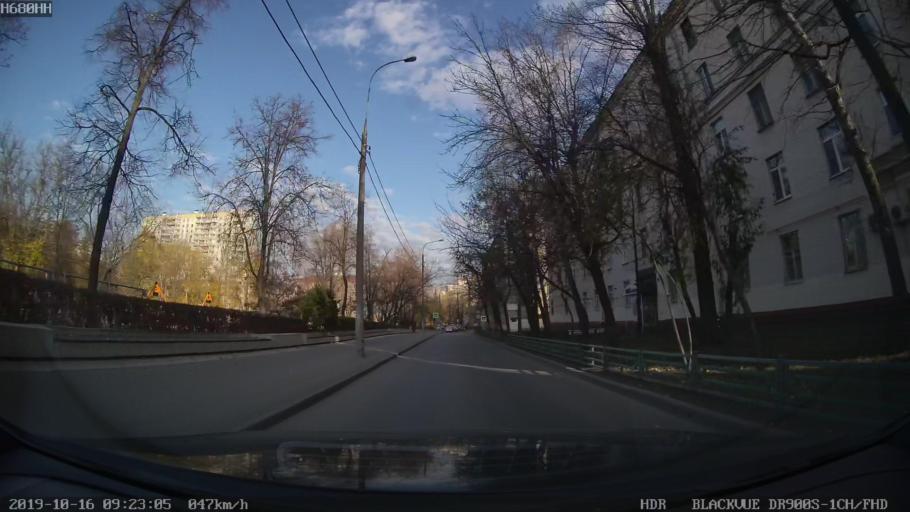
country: RU
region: Moscow
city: Ostankinskiy
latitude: 55.8143
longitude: 37.5901
